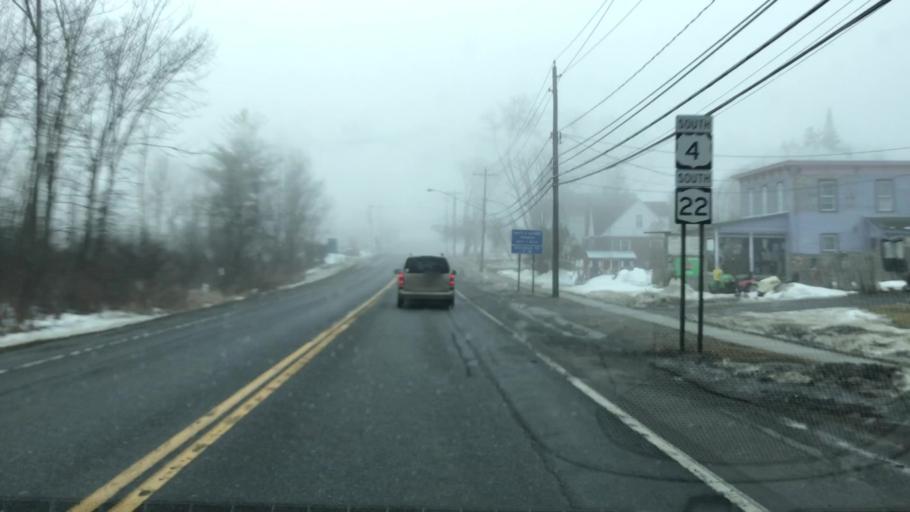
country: US
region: New York
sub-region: Washington County
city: Whitehall
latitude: 43.5422
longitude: -73.4082
